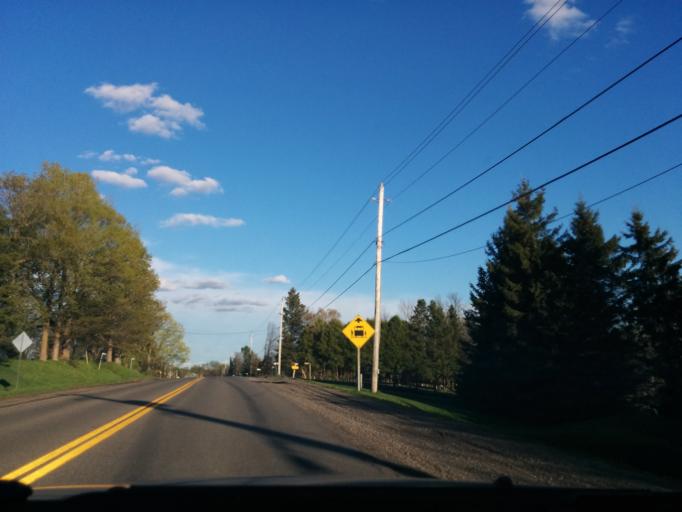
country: CA
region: Ontario
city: Ottawa
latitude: 45.2116
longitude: -75.6528
